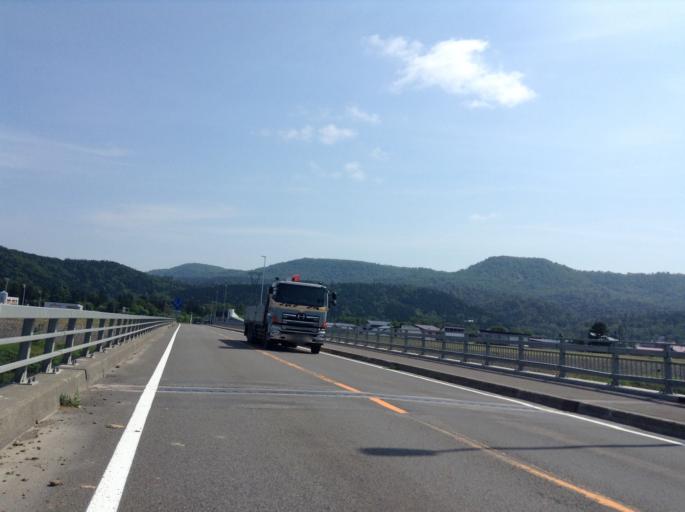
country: JP
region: Hokkaido
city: Nayoro
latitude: 44.7266
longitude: 142.2544
